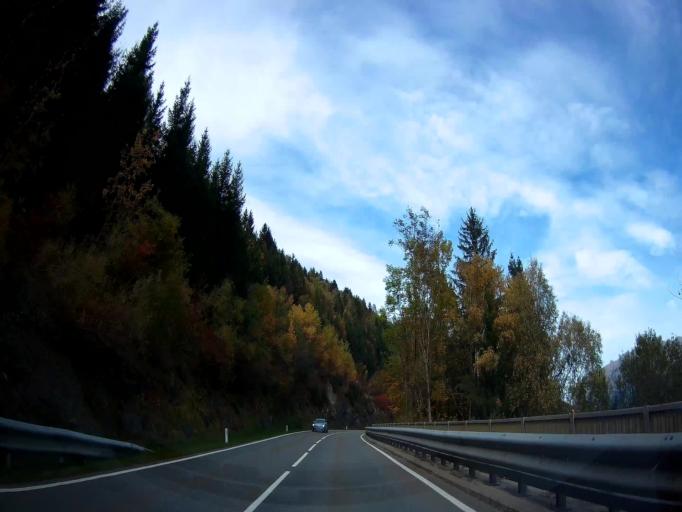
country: AT
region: Salzburg
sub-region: Politischer Bezirk Sankt Johann im Pongau
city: Bischofshofen
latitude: 47.4057
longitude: 13.2136
